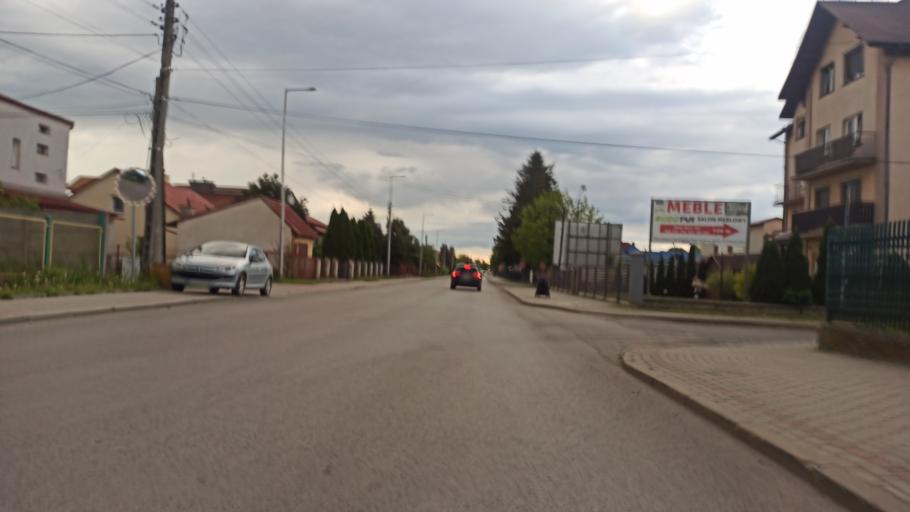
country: PL
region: Subcarpathian Voivodeship
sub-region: Powiat jaroslawski
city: Radymno
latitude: 49.9411
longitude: 22.8311
